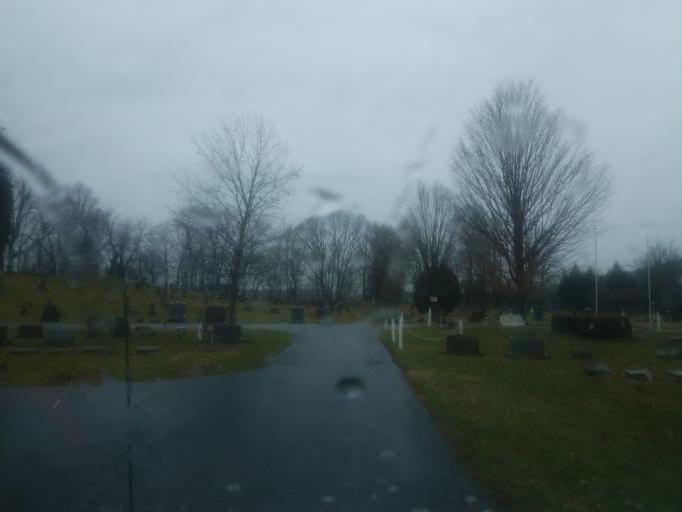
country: US
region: Ohio
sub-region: Sandusky County
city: Bellville
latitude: 40.6221
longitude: -82.5182
